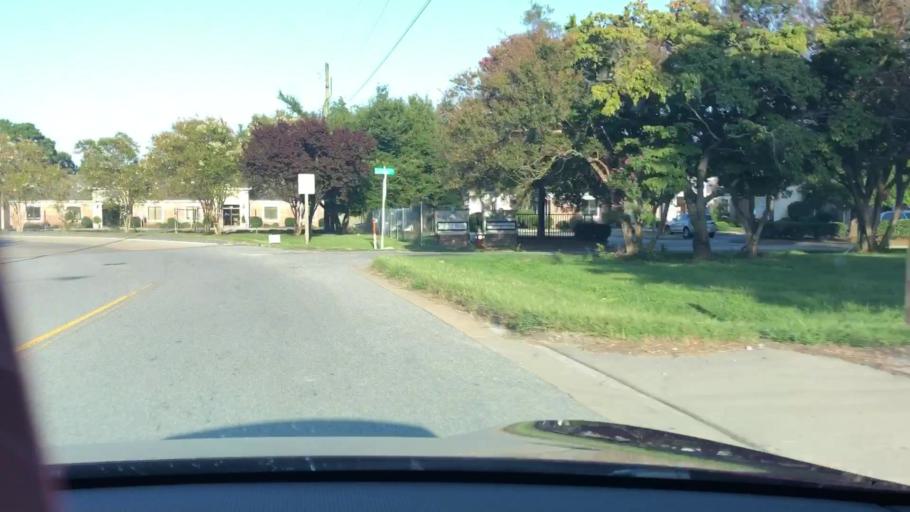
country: US
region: Virginia
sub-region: City of Virginia Beach
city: Virginia Beach
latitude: 36.8440
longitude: -76.0198
